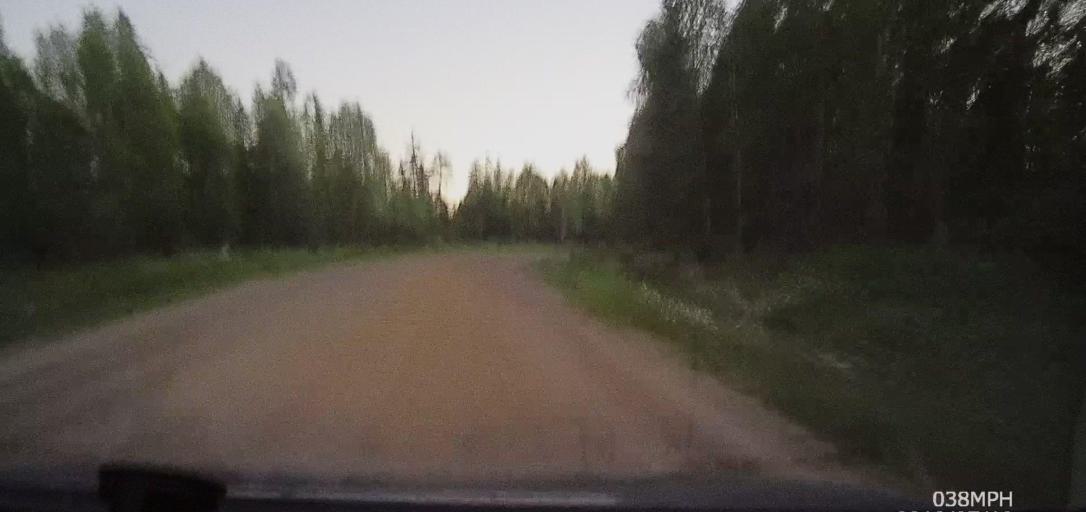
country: RU
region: Arkhangelskaya
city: Pinega
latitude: 64.4235
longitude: 43.1349
